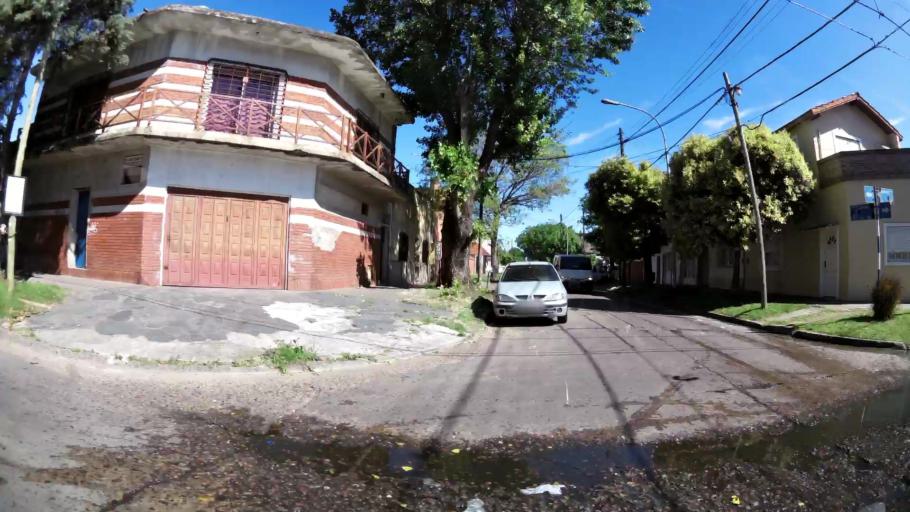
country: AR
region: Buenos Aires
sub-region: Partido de General San Martin
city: General San Martin
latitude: -34.5447
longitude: -58.5281
